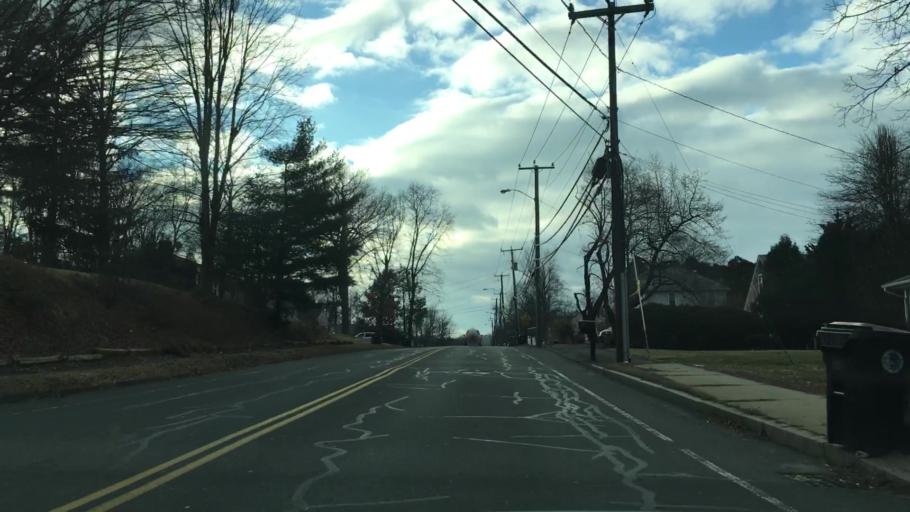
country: US
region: Massachusetts
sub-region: Hampden County
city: Agawam
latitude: 42.0669
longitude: -72.6808
